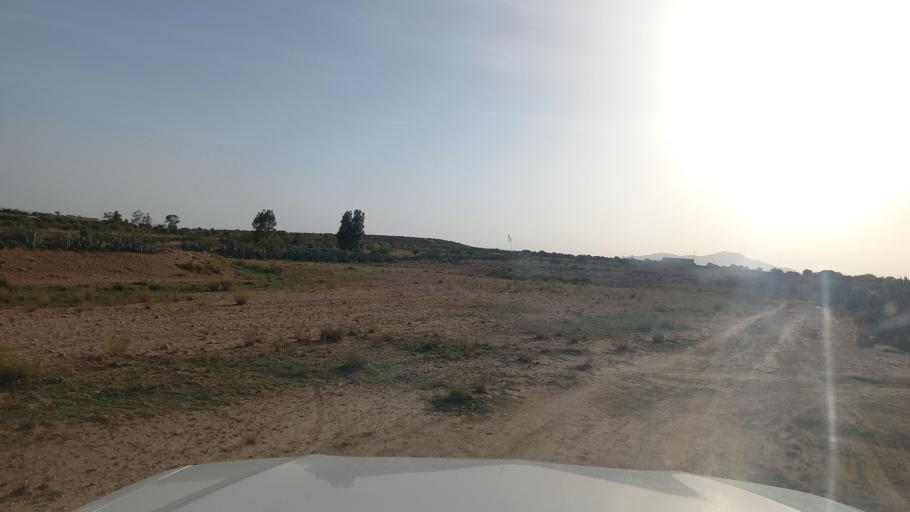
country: TN
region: Al Qasrayn
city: Kasserine
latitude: 35.2571
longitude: 8.9213
